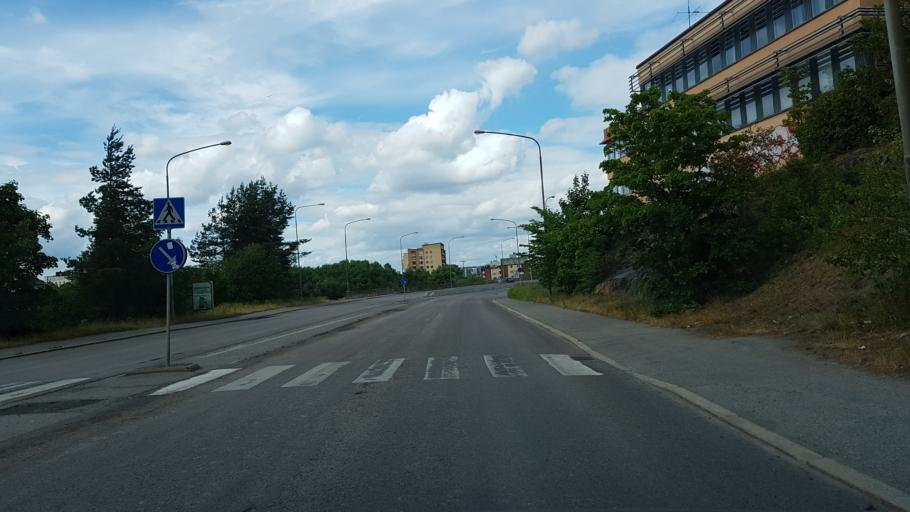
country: SE
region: Stockholm
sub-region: Solna Kommun
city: Solna
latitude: 59.3522
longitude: 17.9902
